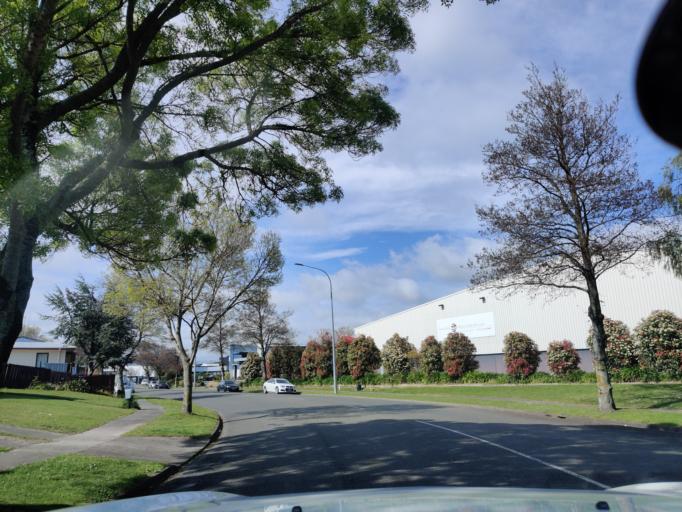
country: NZ
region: Manawatu-Wanganui
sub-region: Palmerston North City
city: Palmerston North
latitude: -40.3331
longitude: 175.6413
